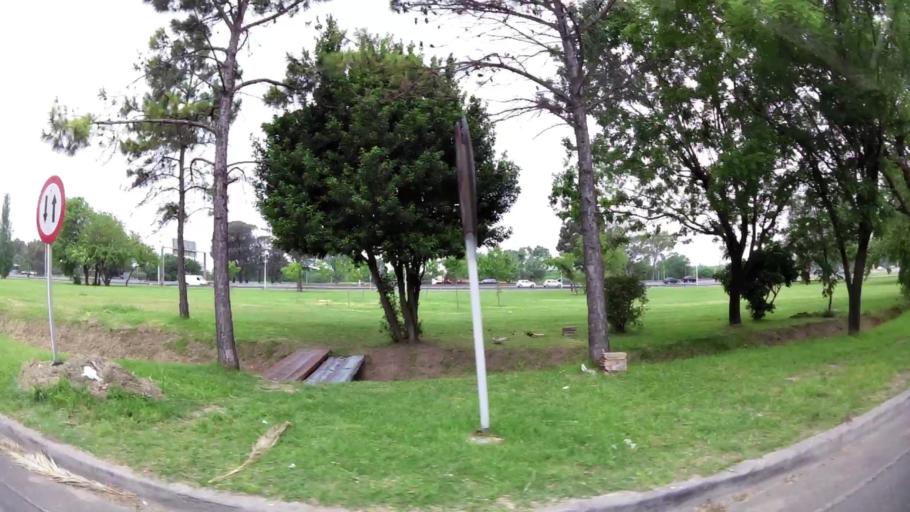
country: AR
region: Buenos Aires
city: San Justo
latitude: -34.7315
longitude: -58.5184
